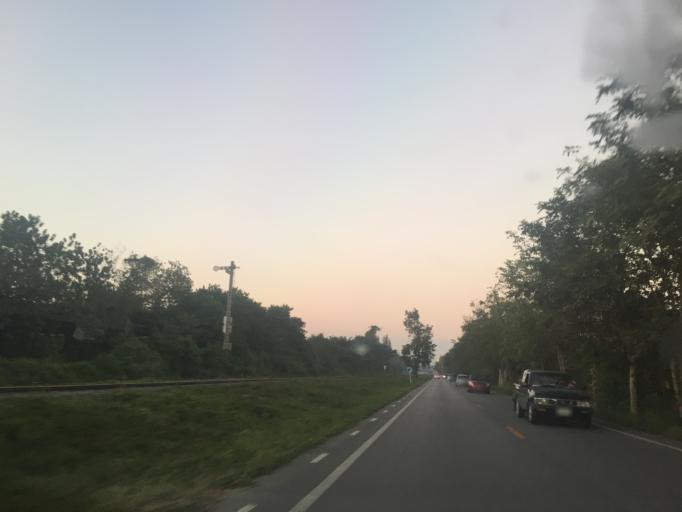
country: TH
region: Lamphun
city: Lamphun
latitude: 18.6327
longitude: 99.0410
